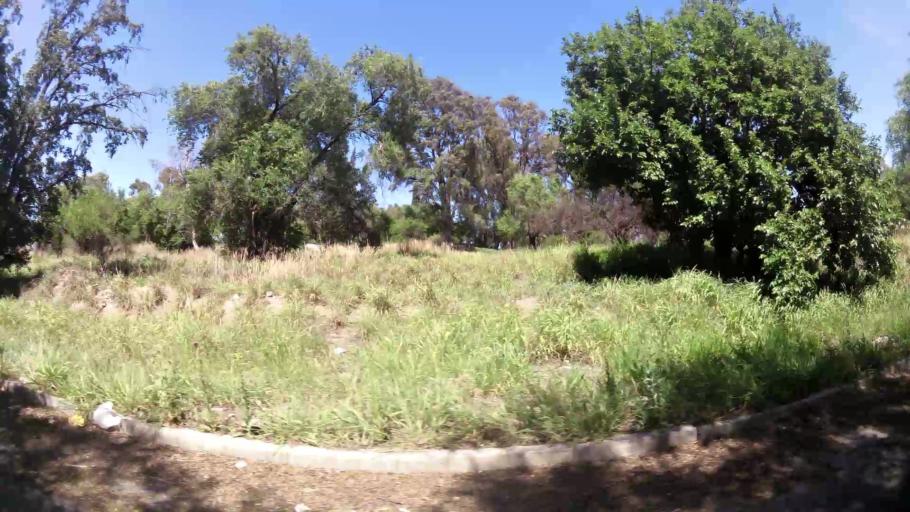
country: AR
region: Cordoba
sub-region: Departamento de Capital
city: Cordoba
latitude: -31.4083
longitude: -64.1317
